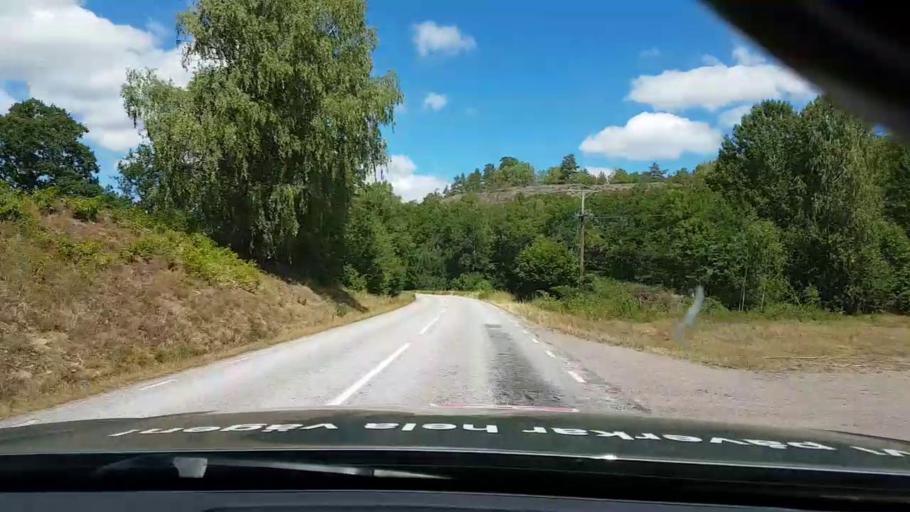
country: SE
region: Kalmar
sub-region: Vasterviks Kommun
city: Overum
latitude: 58.0553
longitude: 16.4060
